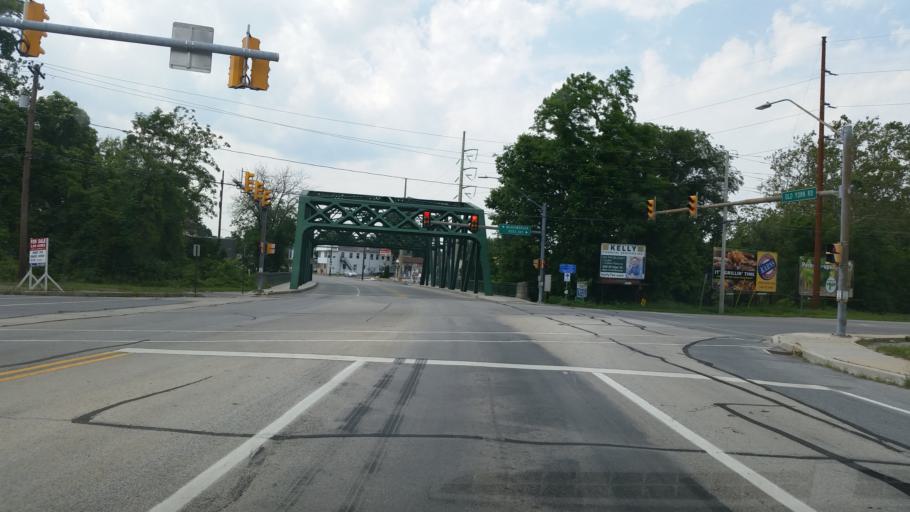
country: US
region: Pennsylvania
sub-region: Dauphin County
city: Steelton
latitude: 40.2236
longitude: -76.8601
